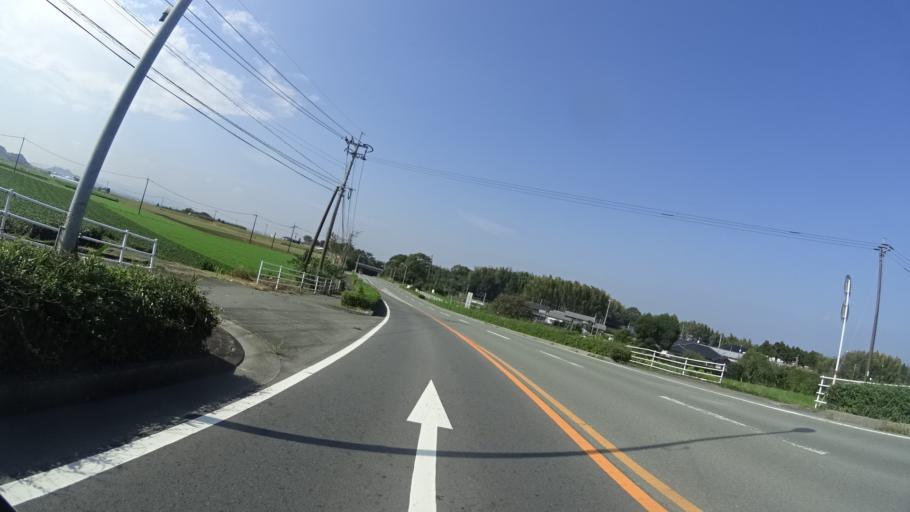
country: JP
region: Kumamoto
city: Ozu
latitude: 32.8492
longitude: 130.8608
